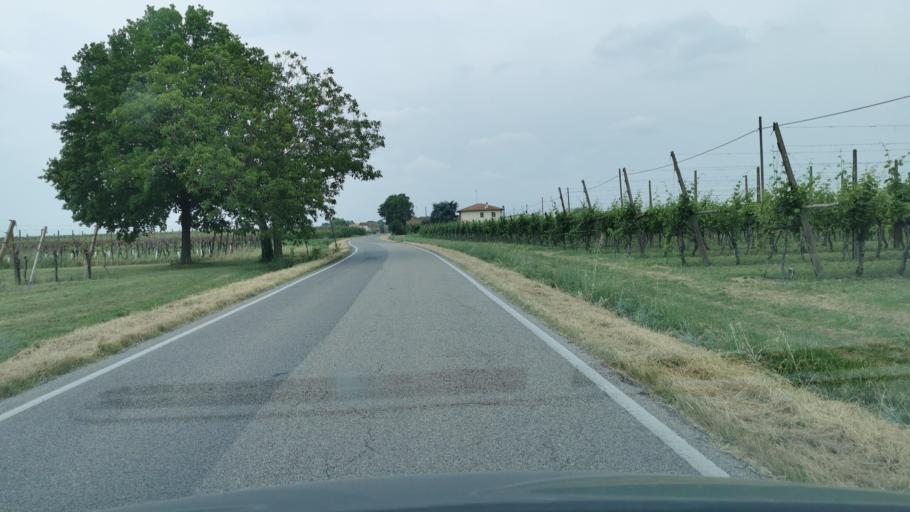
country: IT
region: Emilia-Romagna
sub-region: Provincia di Ravenna
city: Santerno
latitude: 44.4331
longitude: 12.0337
